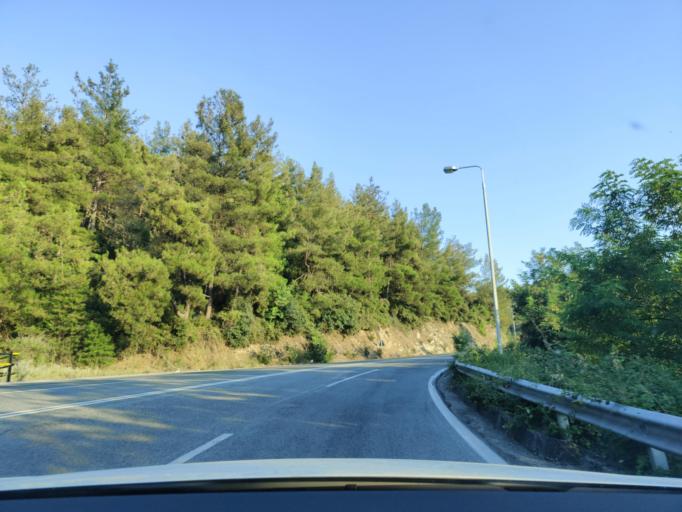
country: GR
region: East Macedonia and Thrace
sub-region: Nomos Kavalas
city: Amygdaleonas
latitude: 40.9481
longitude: 24.3715
